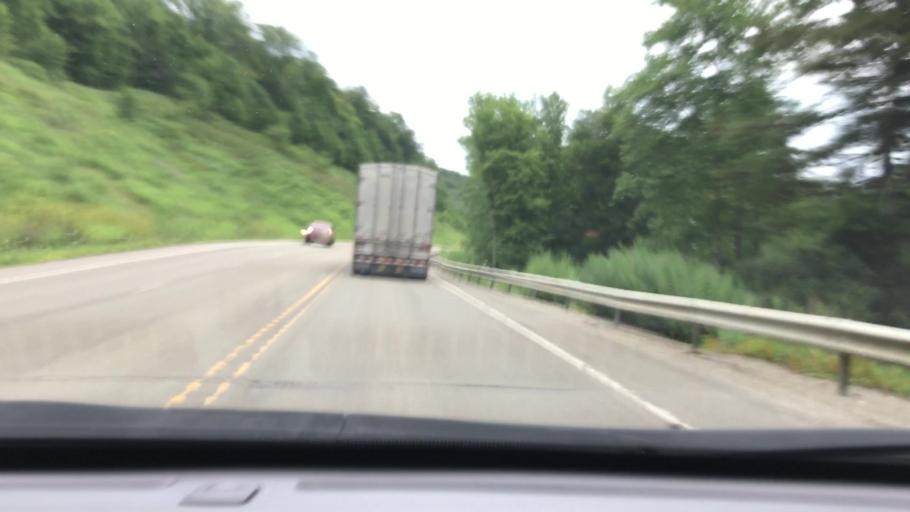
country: US
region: Pennsylvania
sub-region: McKean County
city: Kane
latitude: 41.7502
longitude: -78.6898
